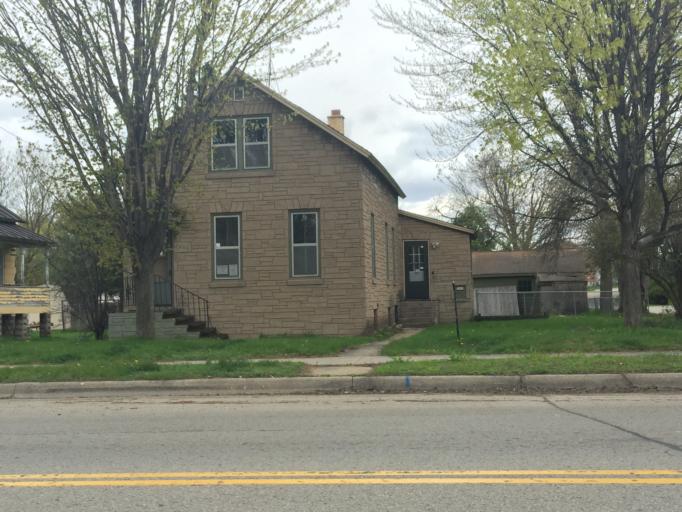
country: US
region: Wisconsin
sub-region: Marinette County
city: Marinette
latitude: 45.1080
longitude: -87.6329
